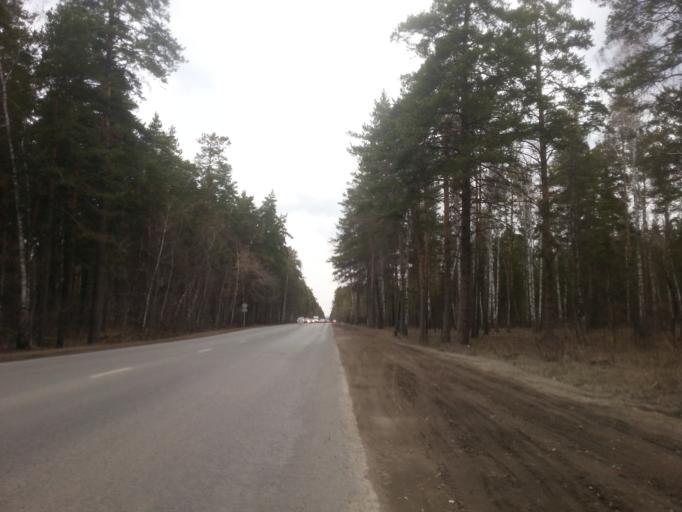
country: RU
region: Altai Krai
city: Yuzhnyy
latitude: 53.2723
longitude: 83.7234
